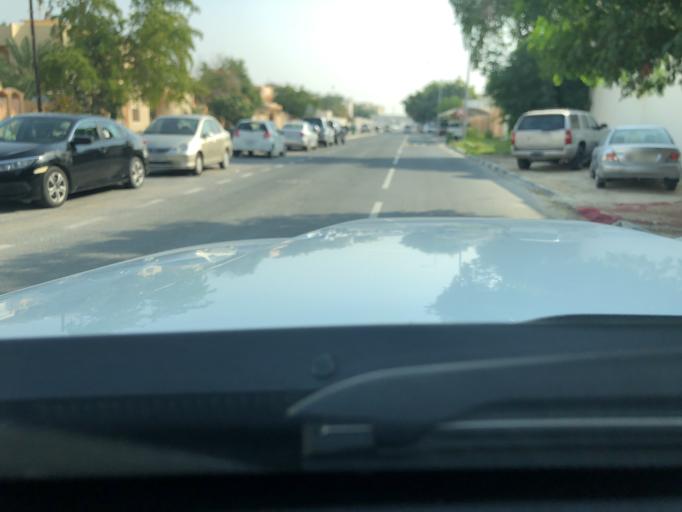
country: QA
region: Baladiyat ar Rayyan
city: Ar Rayyan
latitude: 25.3260
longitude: 51.4749
